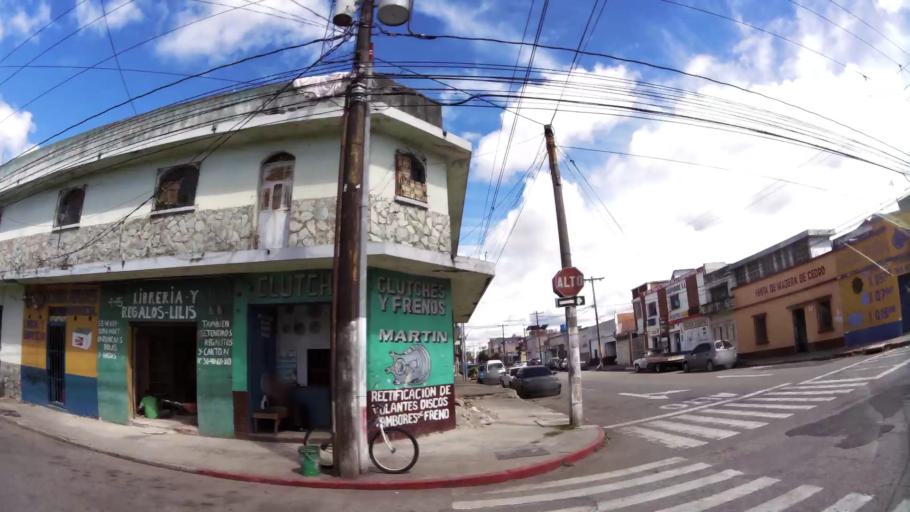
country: GT
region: Guatemala
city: Guatemala City
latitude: 14.6010
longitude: -90.5467
